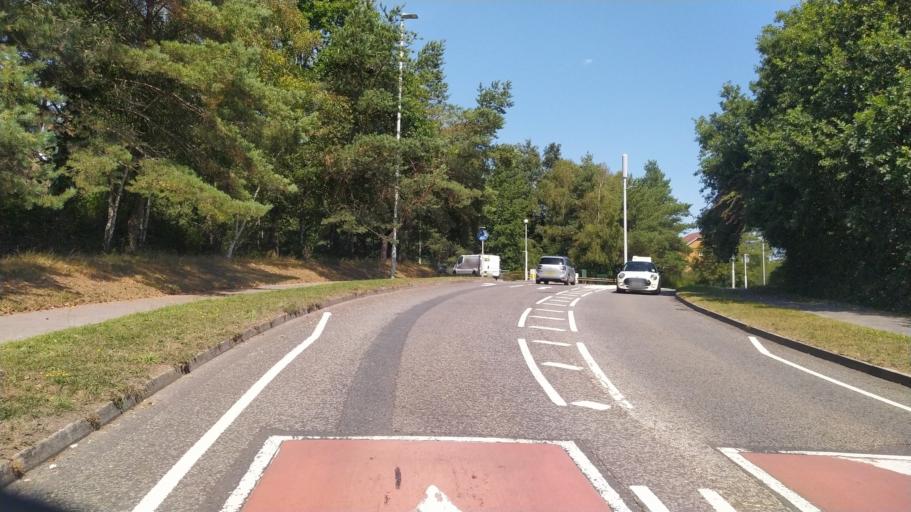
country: GB
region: England
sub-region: Dorset
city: Broadstone
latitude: 50.7509
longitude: -2.0048
